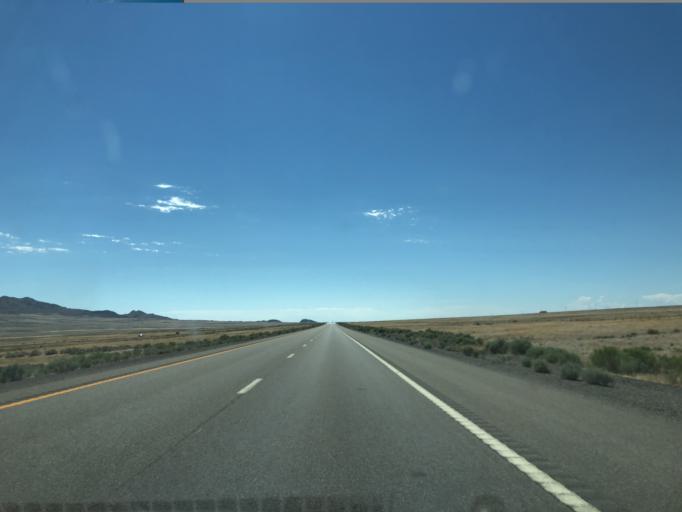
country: US
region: Nevada
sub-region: Elko County
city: West Wendover
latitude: 40.8200
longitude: -114.1876
